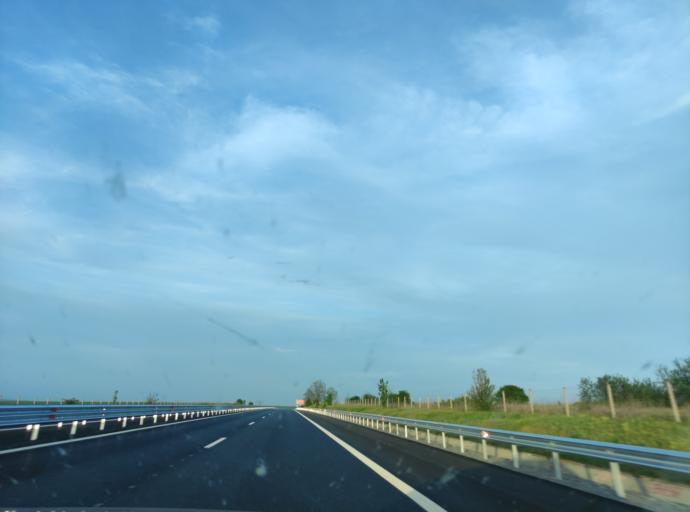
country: BG
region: Stara Zagora
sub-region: Obshtina Chirpan
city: Chirpan
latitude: 42.1946
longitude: 25.2417
